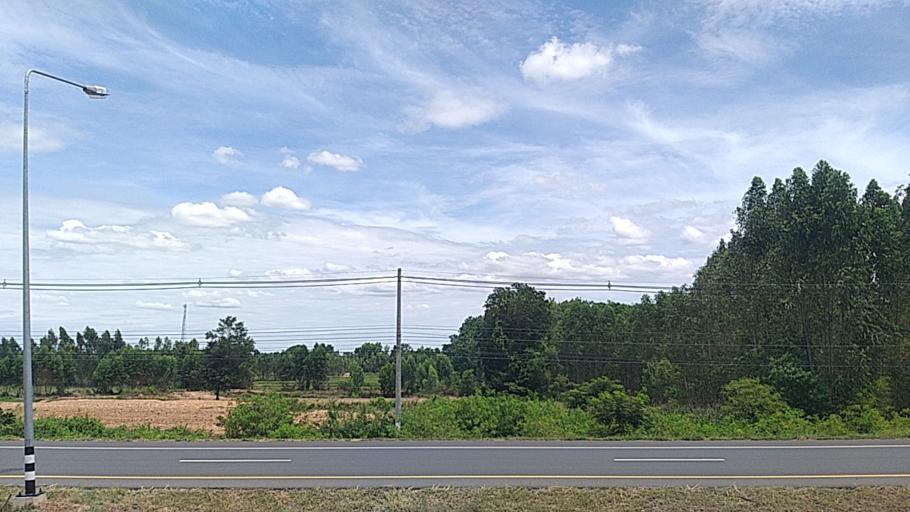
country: TH
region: Buriram
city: Prakhon Chai
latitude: 14.6223
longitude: 103.1834
